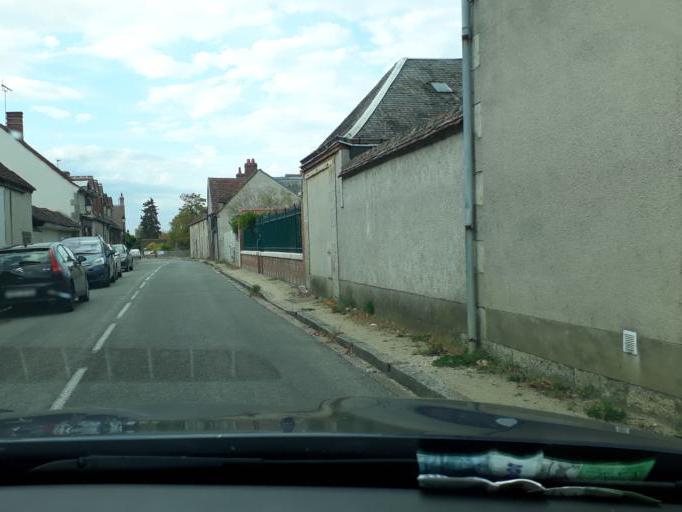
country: FR
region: Centre
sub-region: Departement du Loiret
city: Saint-Benoit-sur-Loire
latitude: 47.8107
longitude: 2.3054
